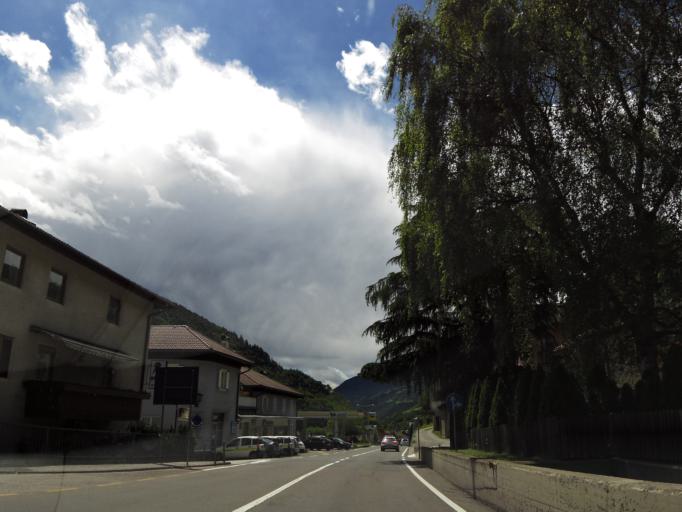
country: IT
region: Trentino-Alto Adige
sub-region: Bolzano
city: Chiusa
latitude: 46.6384
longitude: 11.5617
